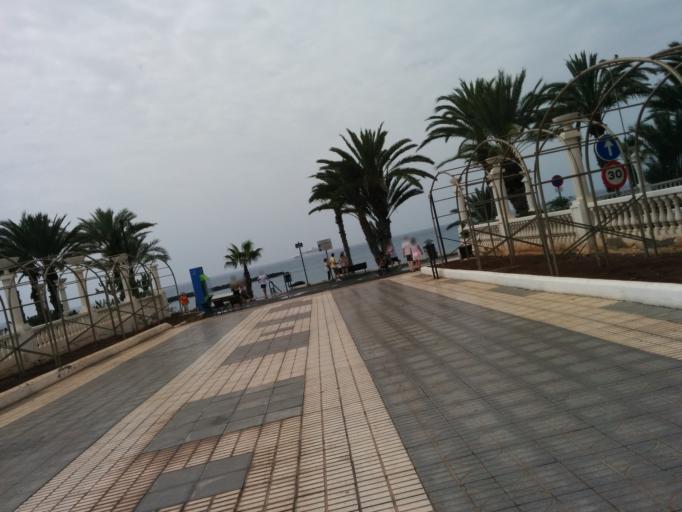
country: ES
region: Canary Islands
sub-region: Provincia de Santa Cruz de Tenerife
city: Playa de las Americas
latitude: 28.0536
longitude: -16.7308
